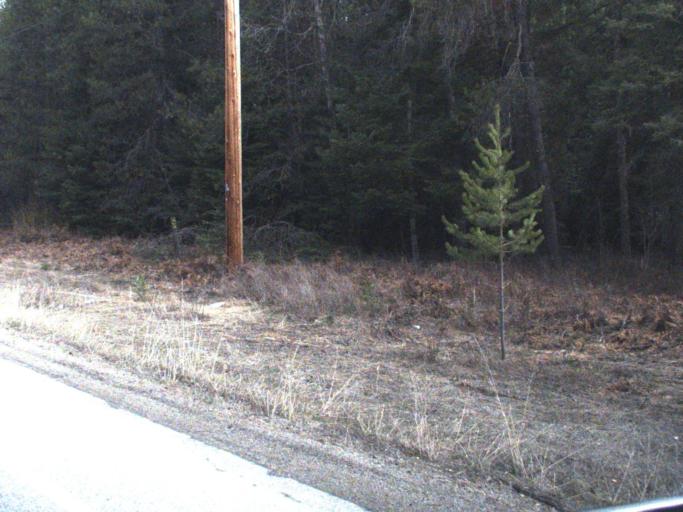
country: US
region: Washington
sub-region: Pend Oreille County
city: Newport
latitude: 48.2693
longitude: -117.2599
